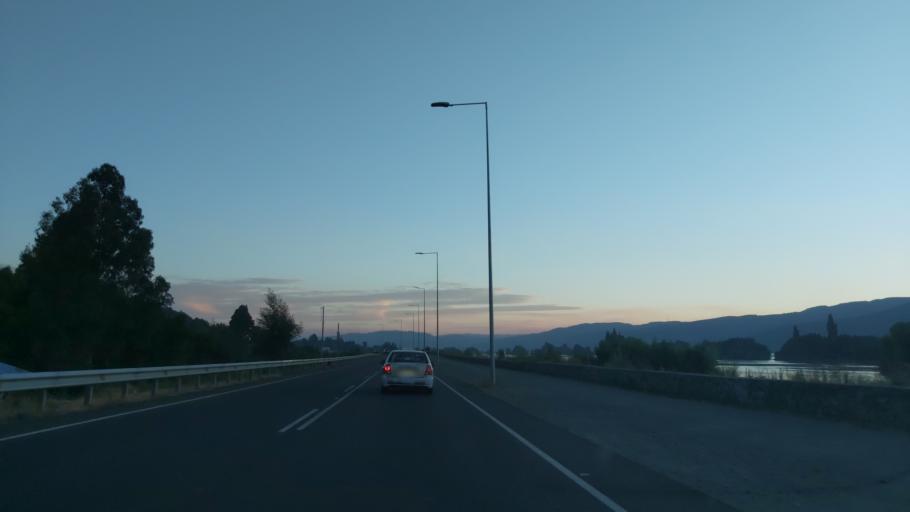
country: CL
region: Biobio
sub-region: Provincia de Concepcion
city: Chiguayante
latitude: -36.8853
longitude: -73.0384
